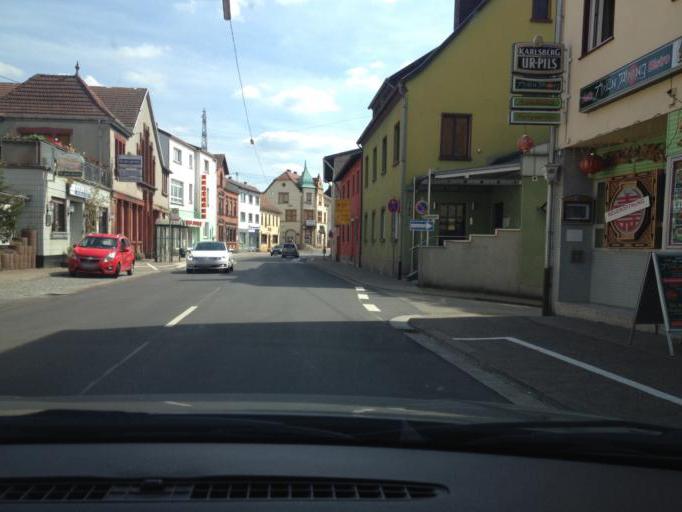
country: DE
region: Saarland
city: Schiffweiler
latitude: 49.3694
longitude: 7.1311
